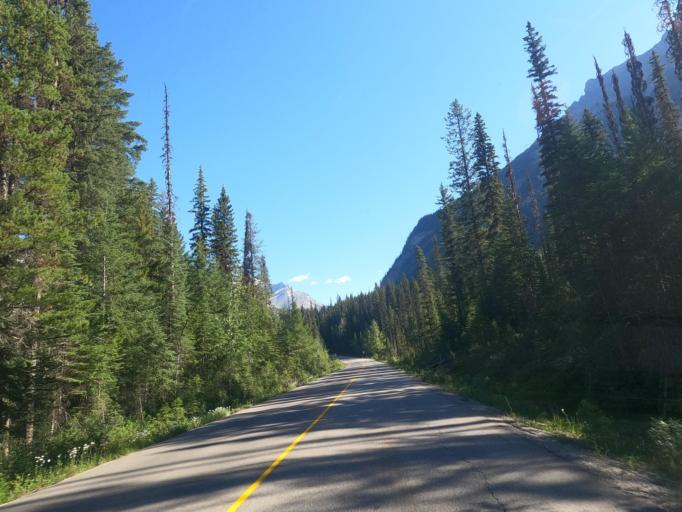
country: CA
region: Alberta
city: Lake Louise
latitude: 51.4097
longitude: -116.5348
